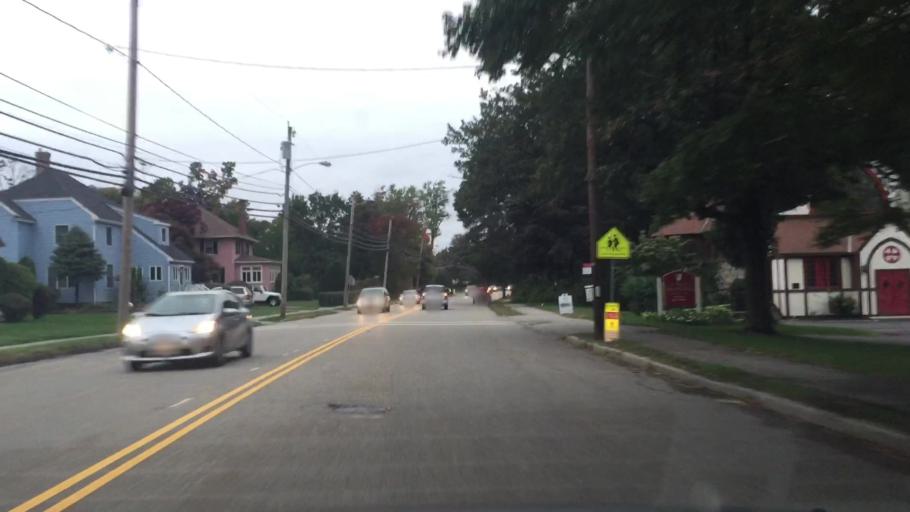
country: US
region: Massachusetts
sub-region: Essex County
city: North Andover
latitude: 42.6942
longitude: -71.1198
